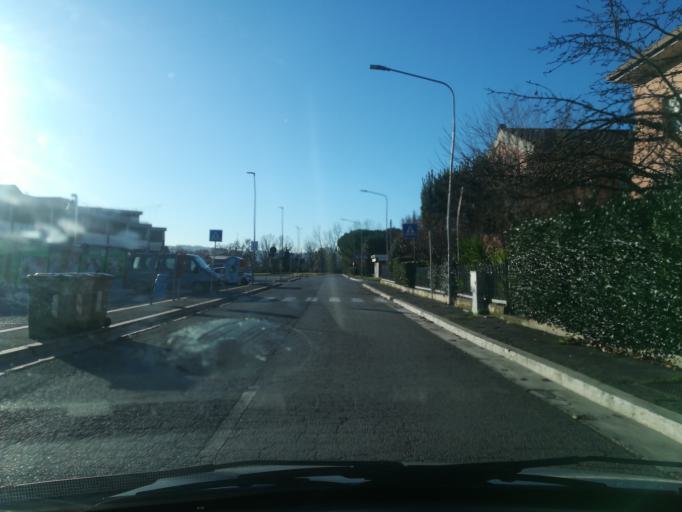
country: IT
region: The Marches
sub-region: Provincia di Macerata
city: Piediripa
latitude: 43.2758
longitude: 13.4796
